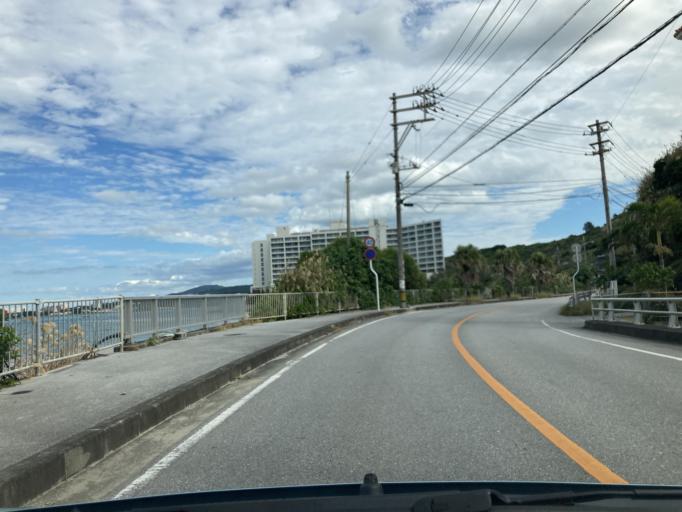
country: JP
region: Okinawa
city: Ishikawa
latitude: 26.4349
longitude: 127.7846
